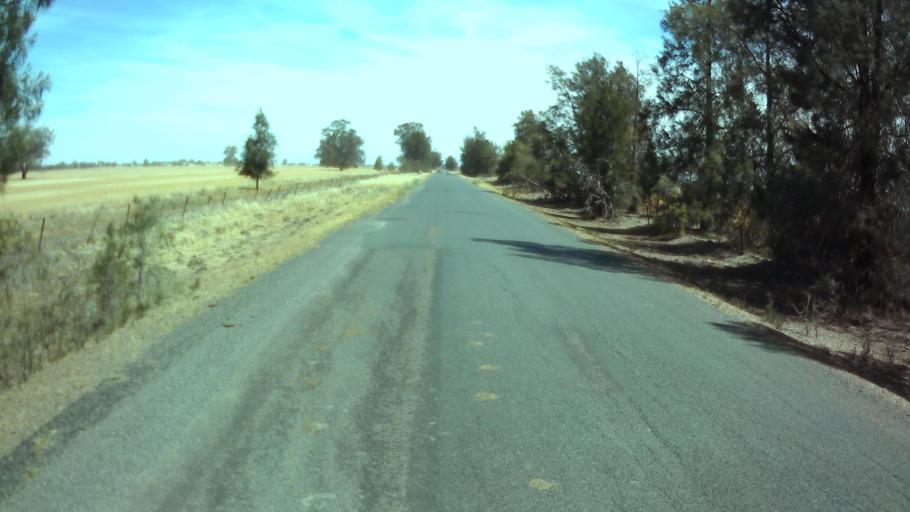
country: AU
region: New South Wales
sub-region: Weddin
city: Grenfell
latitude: -33.9226
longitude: 147.7638
